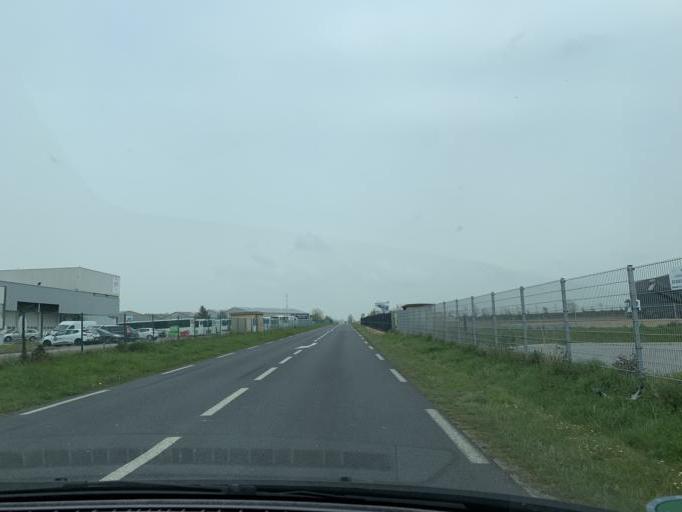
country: FR
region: Haute-Normandie
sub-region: Departement de la Seine-Maritime
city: Martin-Eglise
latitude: 49.9221
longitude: 1.1174
